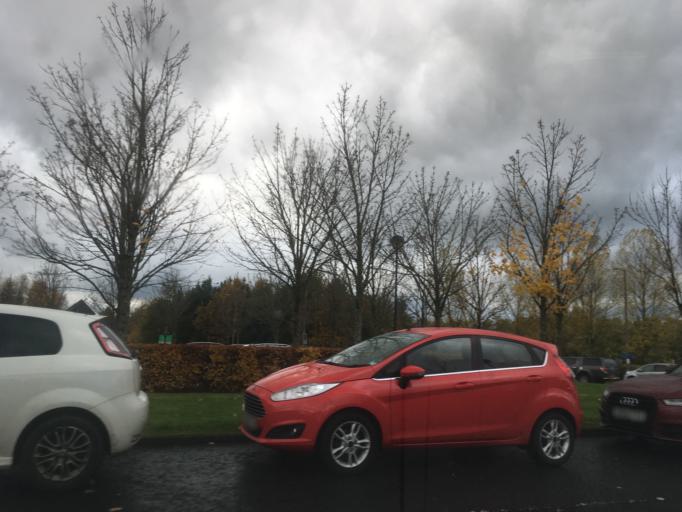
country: GB
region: Scotland
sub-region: Stirling
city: Bridge of Allan
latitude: 56.1318
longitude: -3.9624
